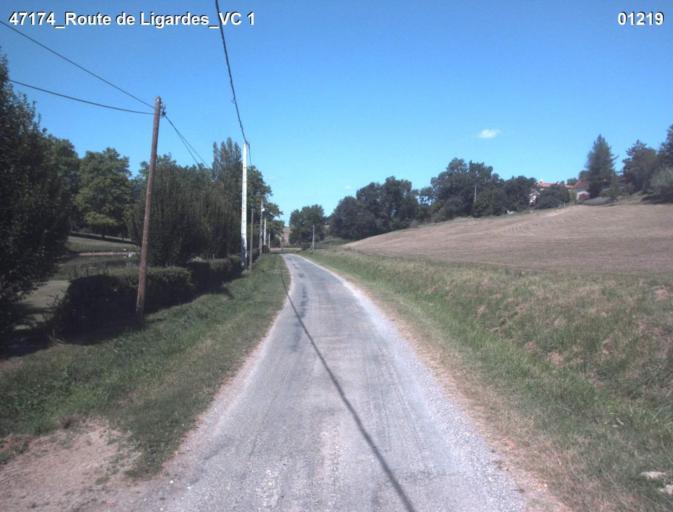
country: FR
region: Midi-Pyrenees
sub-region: Departement du Gers
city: Condom
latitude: 44.0332
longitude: 0.4057
